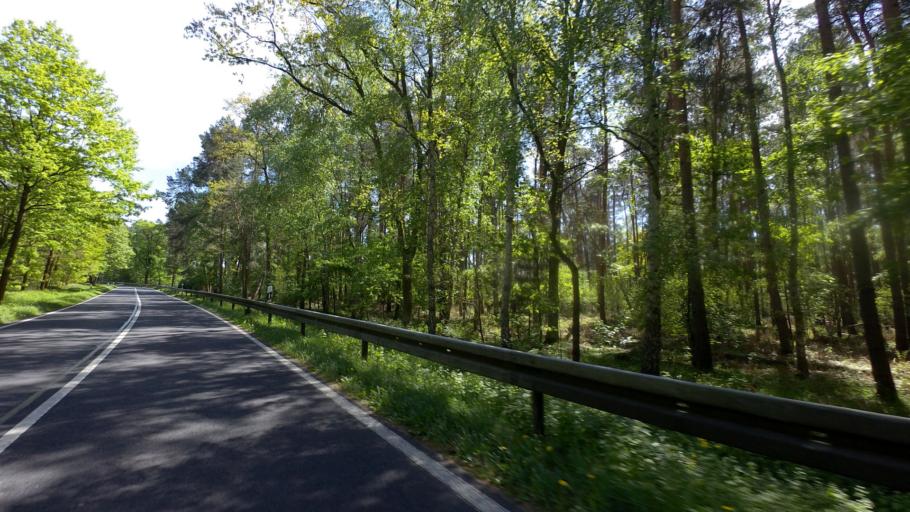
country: DE
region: Brandenburg
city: Luckenwalde
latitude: 52.0500
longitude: 13.2575
